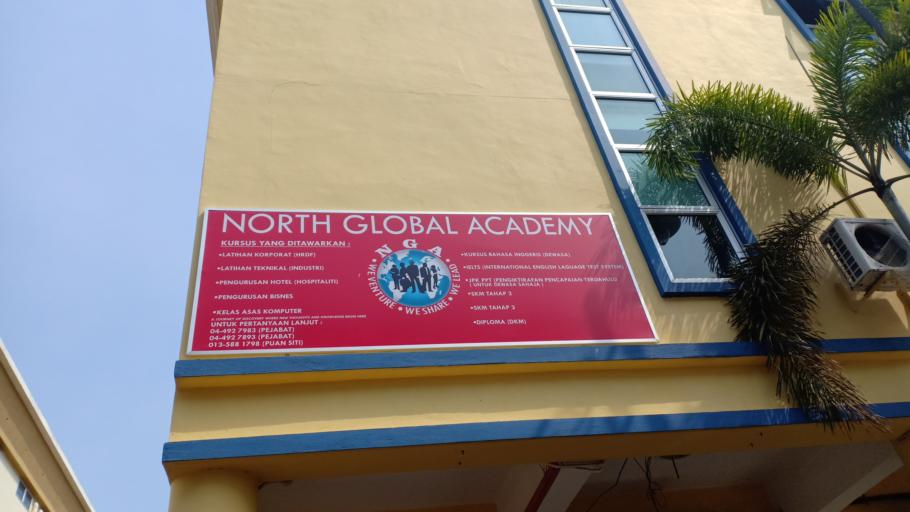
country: MY
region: Kedah
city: Kulim
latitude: 5.3688
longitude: 100.5550
